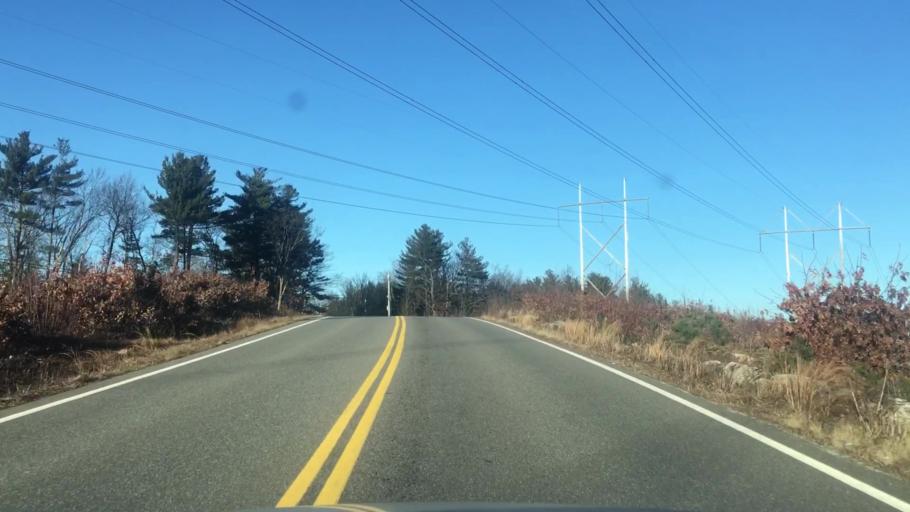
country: US
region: New Hampshire
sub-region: Rockingham County
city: Londonderry
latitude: 42.8894
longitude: -71.3695
